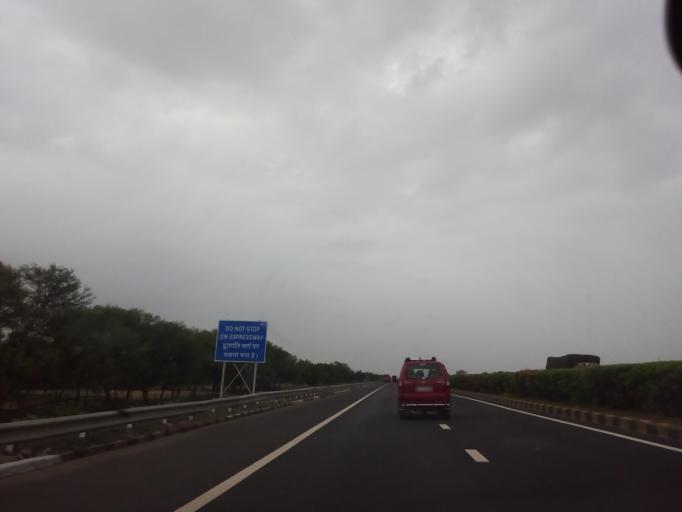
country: IN
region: Gujarat
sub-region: Kheda
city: Mahemdavad
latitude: 22.8426
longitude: 72.8183
